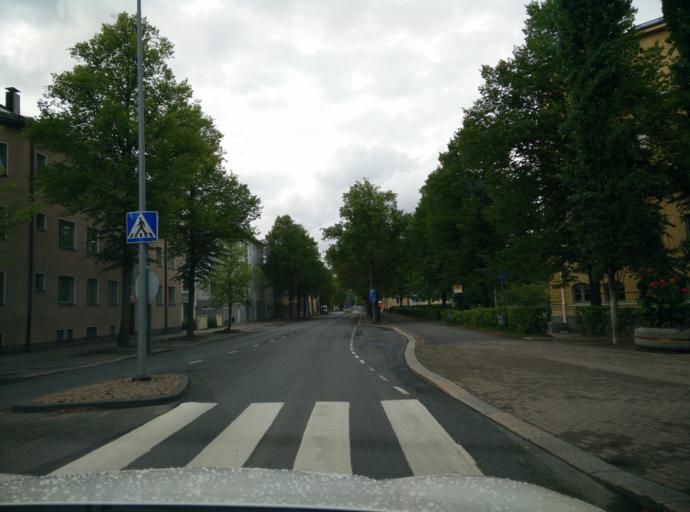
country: FI
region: Haeme
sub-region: Haemeenlinna
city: Haemeenlinna
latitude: 60.9947
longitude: 24.4510
